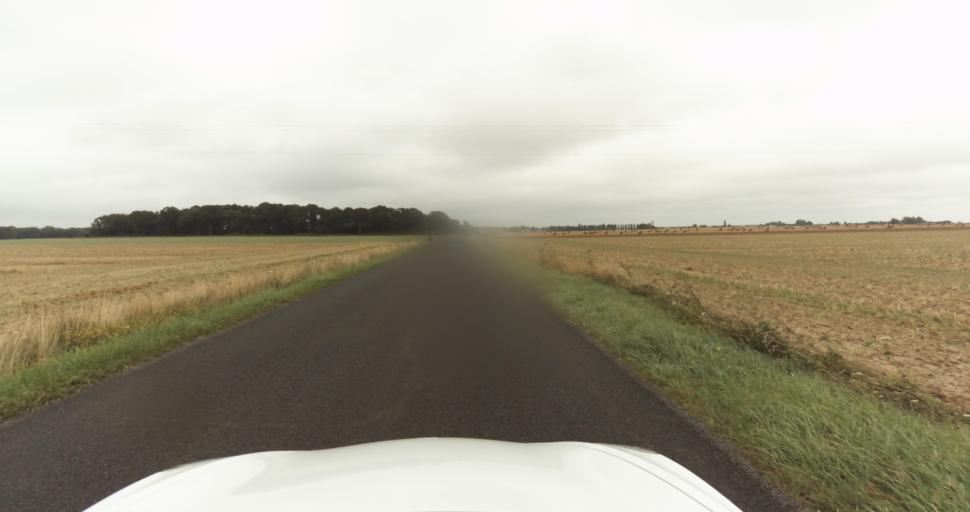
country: FR
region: Haute-Normandie
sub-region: Departement de l'Eure
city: Claville
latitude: 49.0896
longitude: 1.0583
